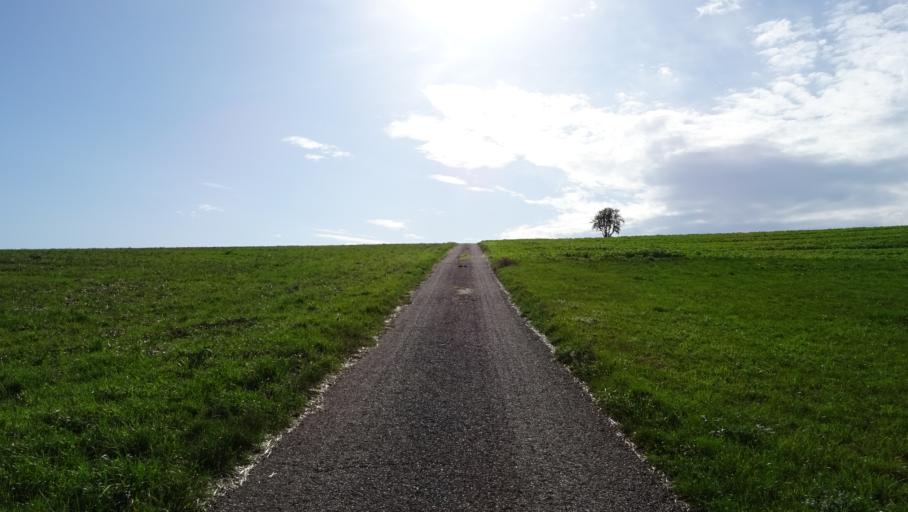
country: DE
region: Baden-Wuerttemberg
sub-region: Karlsruhe Region
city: Billigheim
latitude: 49.3630
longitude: 9.2752
